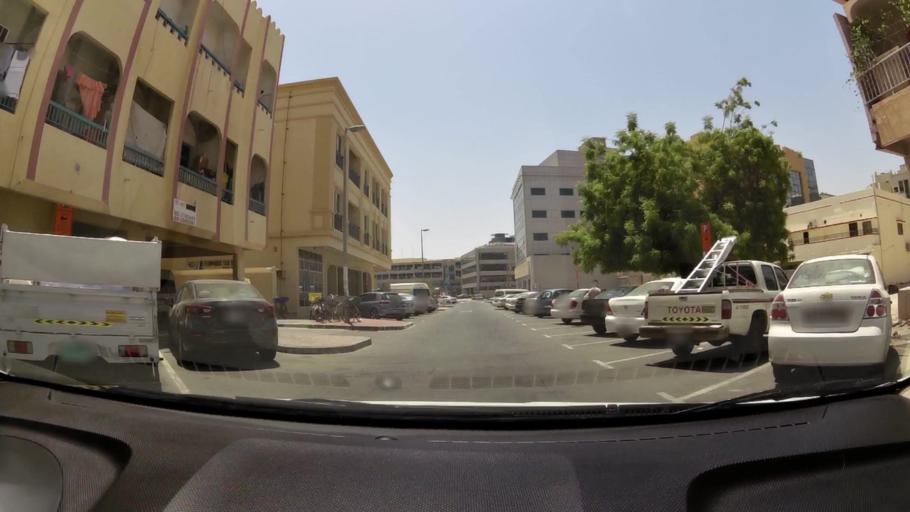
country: AE
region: Ash Shariqah
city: Sharjah
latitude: 25.2612
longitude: 55.3304
